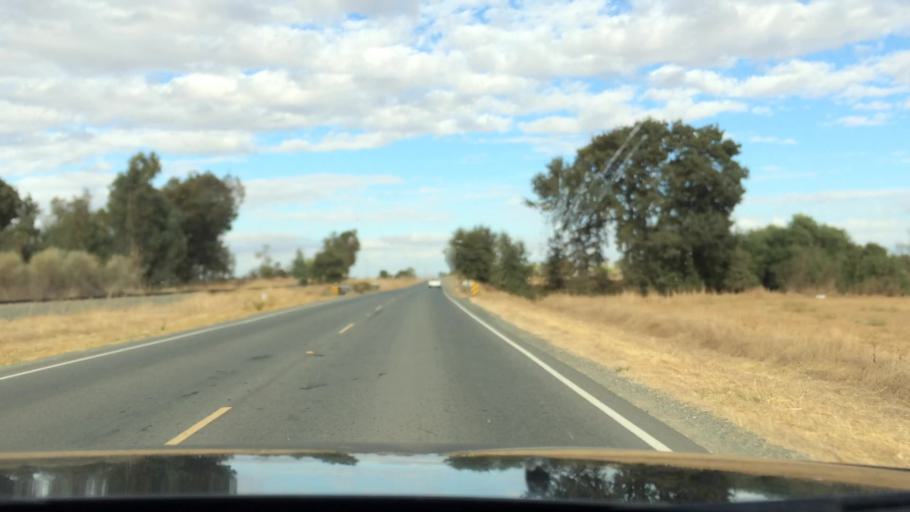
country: US
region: California
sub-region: Sacramento County
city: Herald
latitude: 38.2995
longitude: -121.2376
